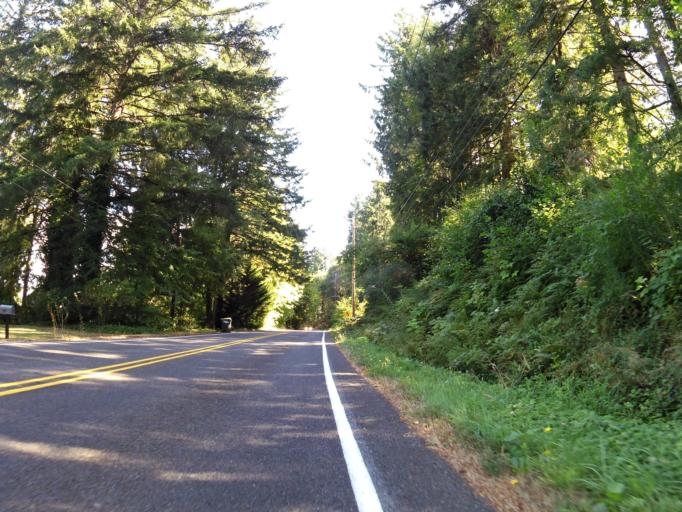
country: US
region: Washington
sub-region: Thurston County
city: Olympia
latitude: 47.0647
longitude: -123.0167
